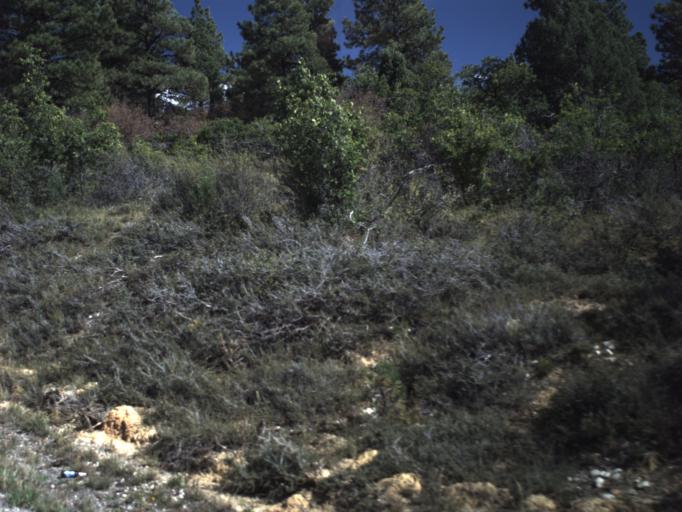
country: US
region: Utah
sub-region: Garfield County
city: Panguitch
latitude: 37.4958
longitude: -112.5508
